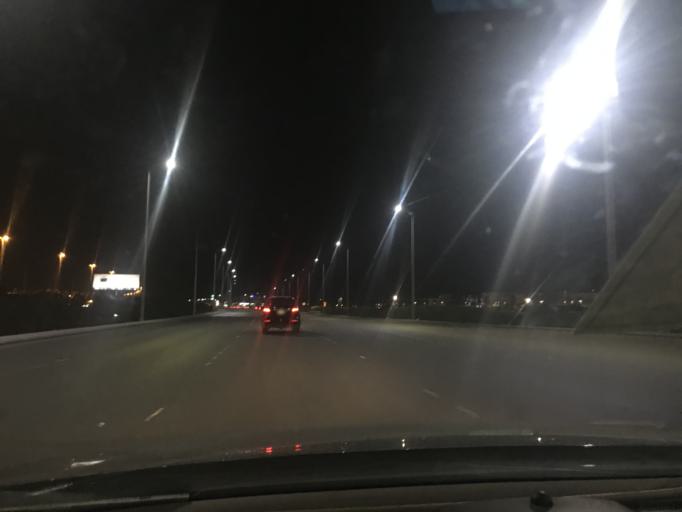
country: SA
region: Ar Riyad
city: Riyadh
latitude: 24.8389
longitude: 46.7295
